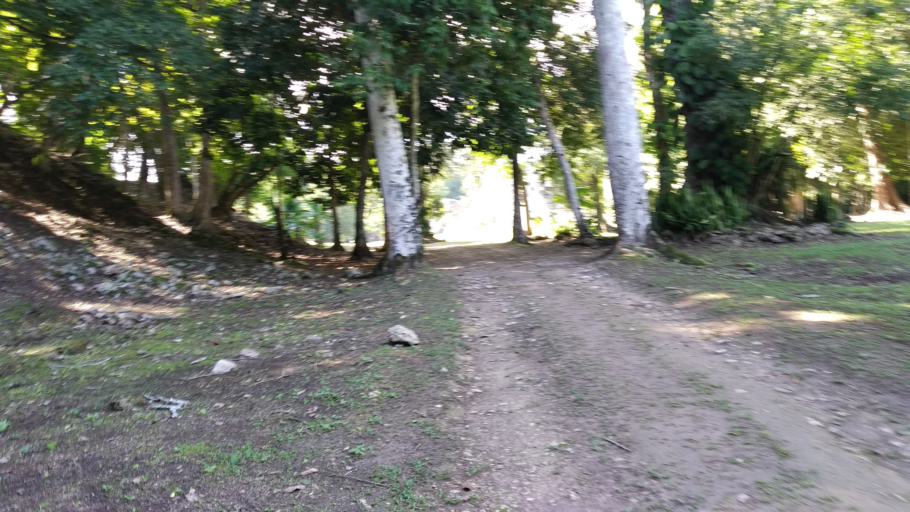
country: GT
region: Peten
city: Melchor de Mencos
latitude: 16.7627
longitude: -89.1189
